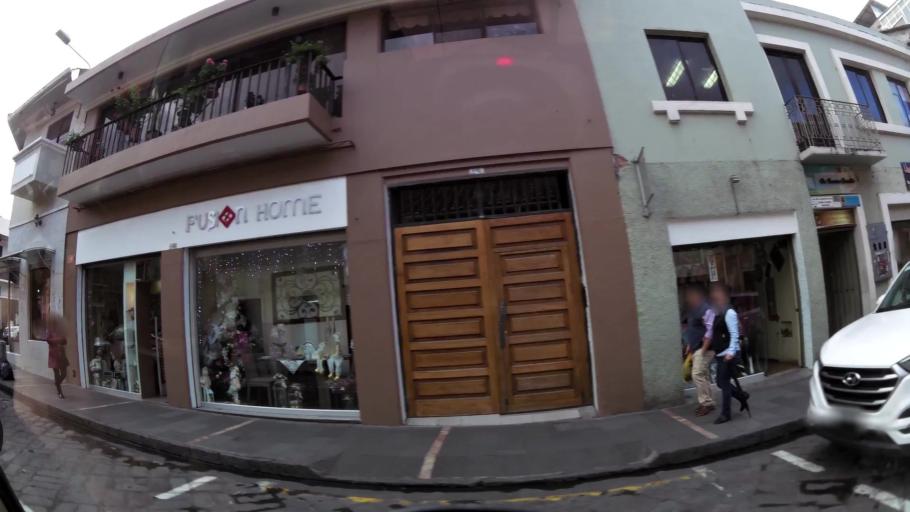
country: EC
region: Azuay
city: Cuenca
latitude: -2.8978
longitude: -79.0007
